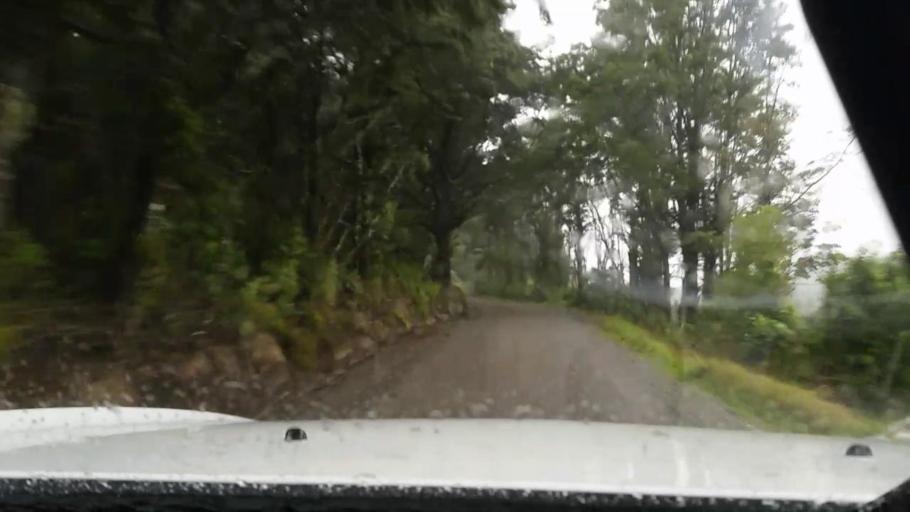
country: NZ
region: Wellington
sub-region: Masterton District
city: Masterton
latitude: -41.1843
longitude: 175.8228
